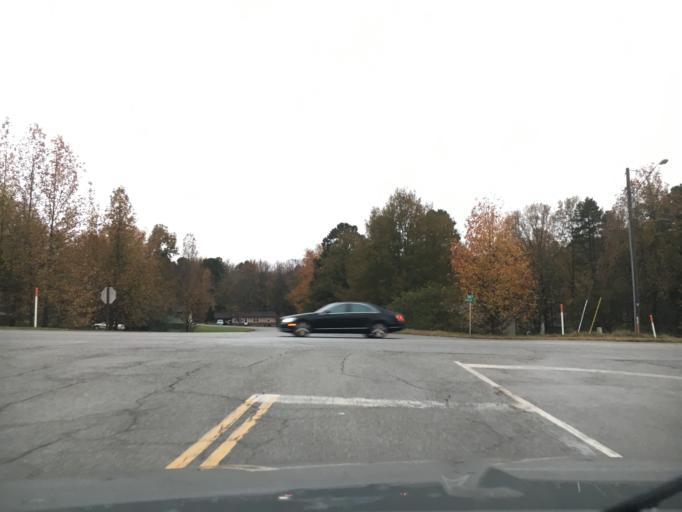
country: US
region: Virginia
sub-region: Halifax County
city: South Boston
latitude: 36.7150
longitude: -78.8923
